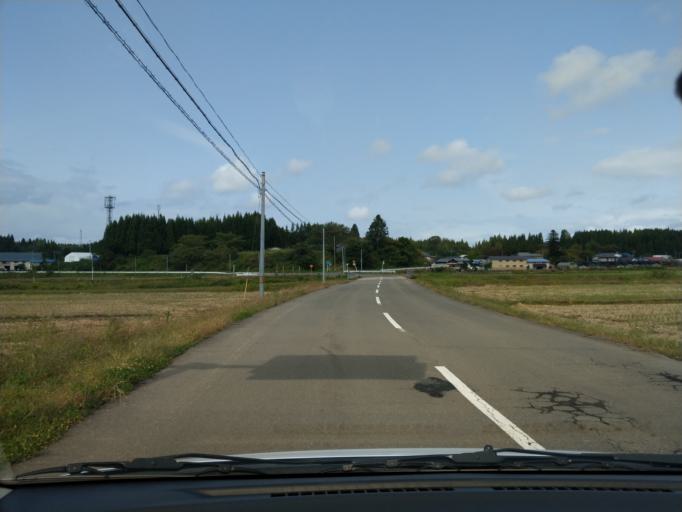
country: JP
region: Akita
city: Omagari
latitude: 39.5177
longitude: 140.3053
